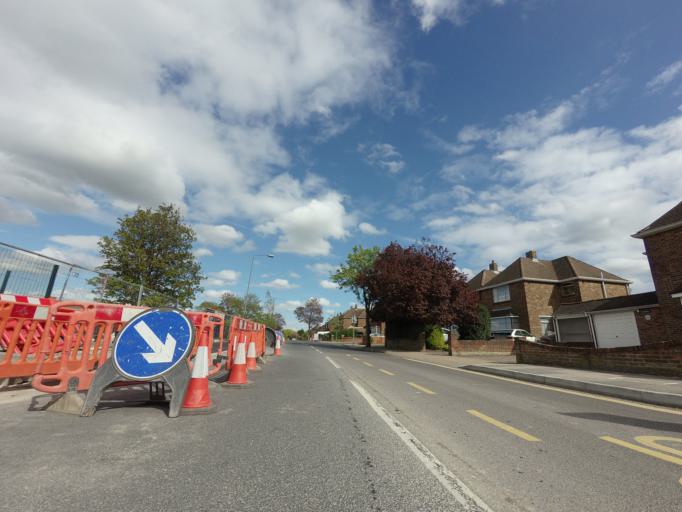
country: GB
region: England
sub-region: Greater London
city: Orpington
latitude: 51.3696
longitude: 0.1182
